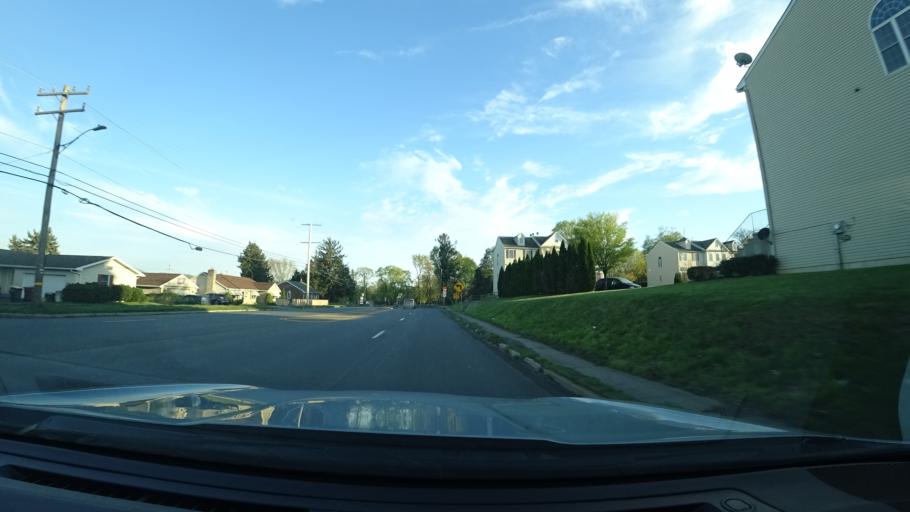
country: US
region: Pennsylvania
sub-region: Lehigh County
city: Fullerton
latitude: 40.6277
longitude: -75.4698
